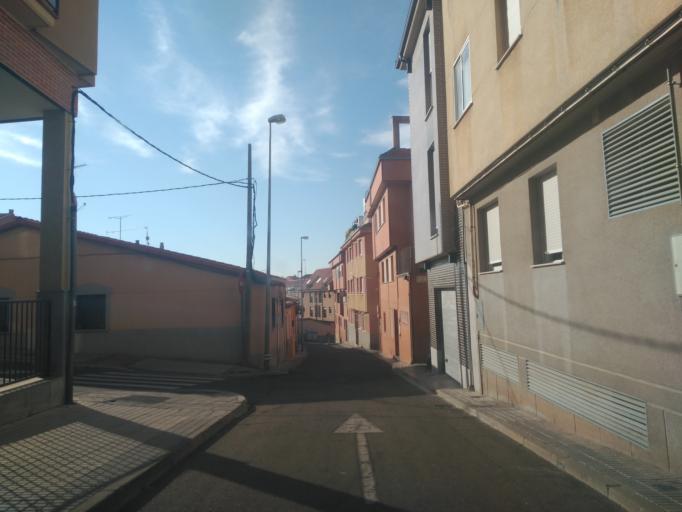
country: ES
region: Castille and Leon
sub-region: Provincia de Salamanca
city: Salamanca
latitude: 40.9778
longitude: -5.6753
